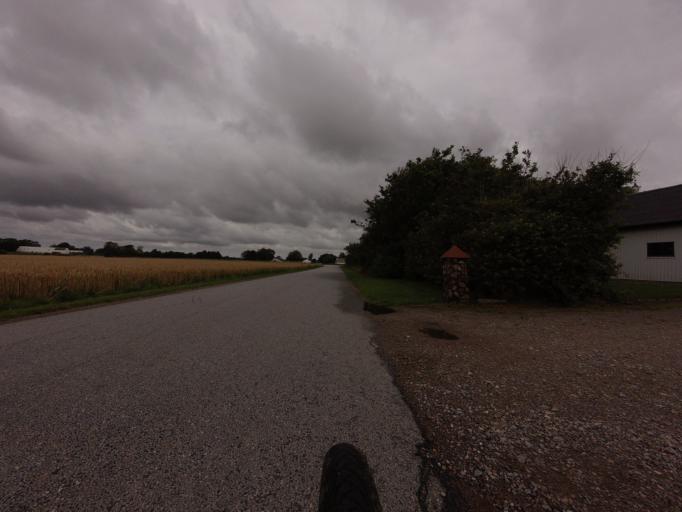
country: DK
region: North Denmark
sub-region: Bronderslev Kommune
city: Bronderslev
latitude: 57.3048
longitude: 9.8068
